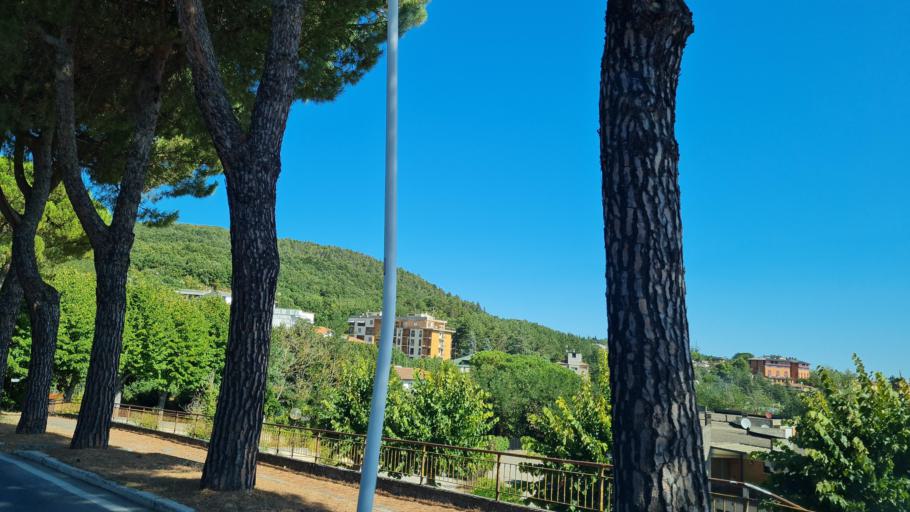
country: IT
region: Tuscany
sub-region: Provincia di Siena
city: Chianciano Terme
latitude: 43.0422
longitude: 11.8125
